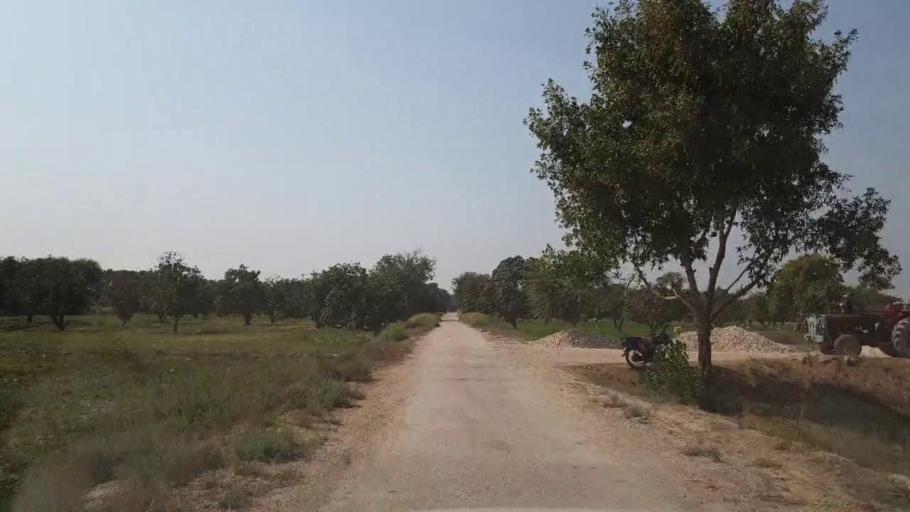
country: PK
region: Sindh
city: Mirpur Khas
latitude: 25.6266
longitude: 69.1062
